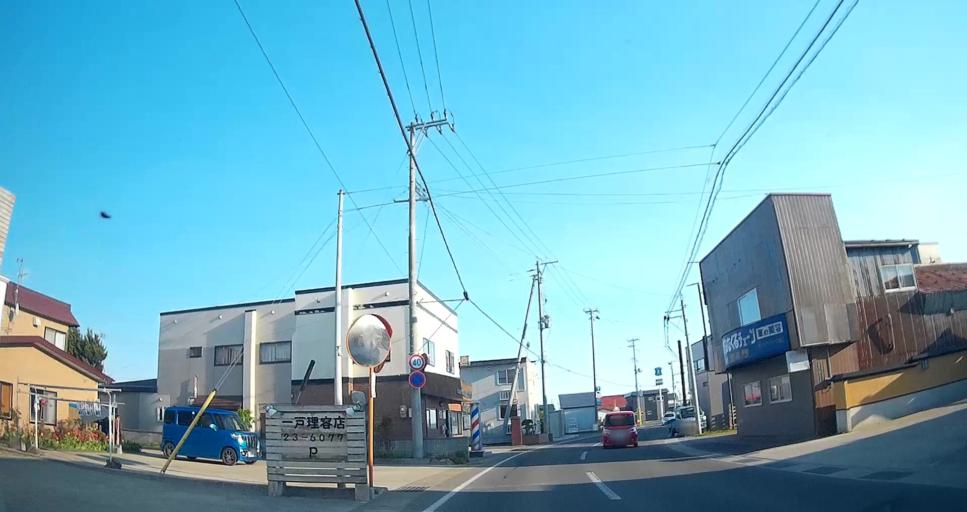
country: JP
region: Aomori
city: Mutsu
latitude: 41.2870
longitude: 141.2116
